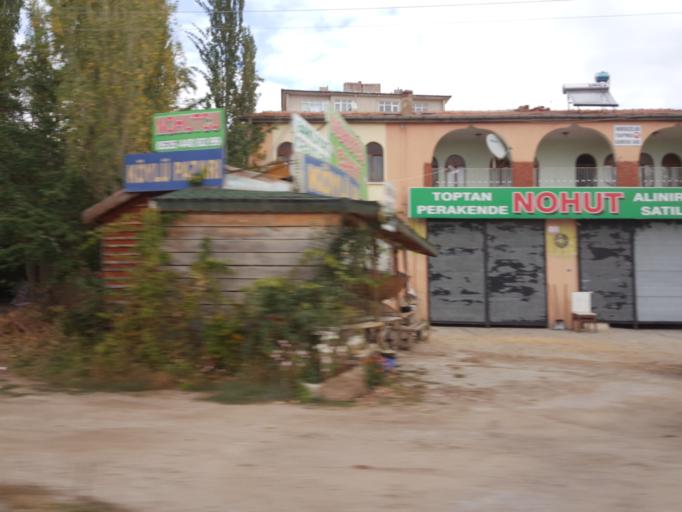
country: TR
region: Kirikkale
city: Keskin
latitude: 39.6733
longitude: 33.6059
